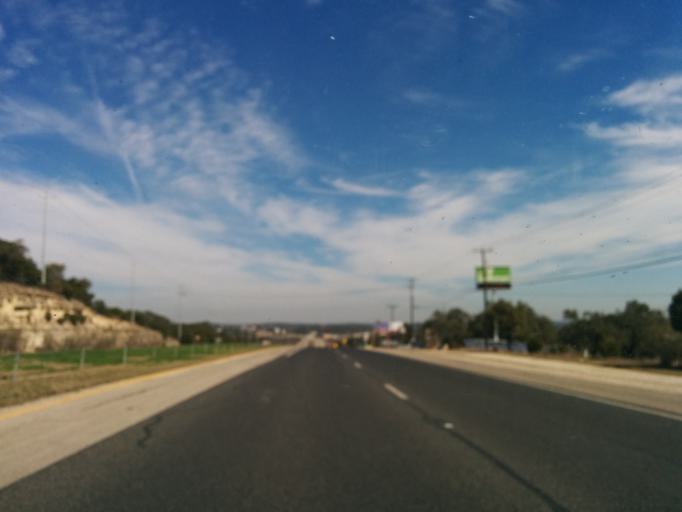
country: US
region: Texas
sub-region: Comal County
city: Bulverde
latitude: 29.7126
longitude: -98.4473
